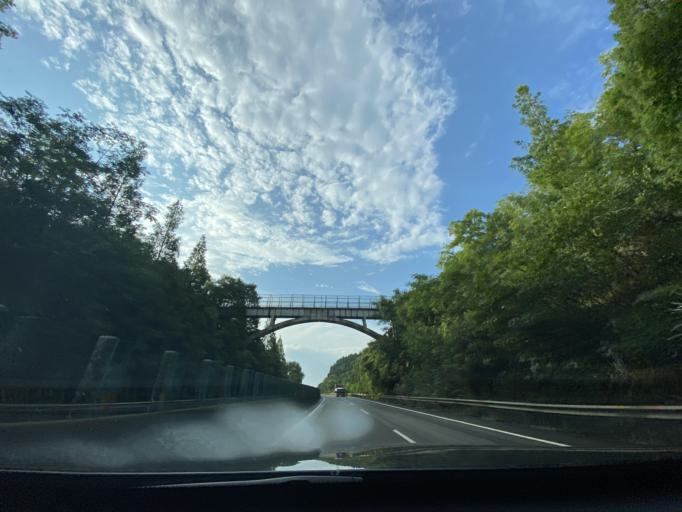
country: CN
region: Sichuan
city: Jiancheng
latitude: 30.3144
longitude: 104.5769
